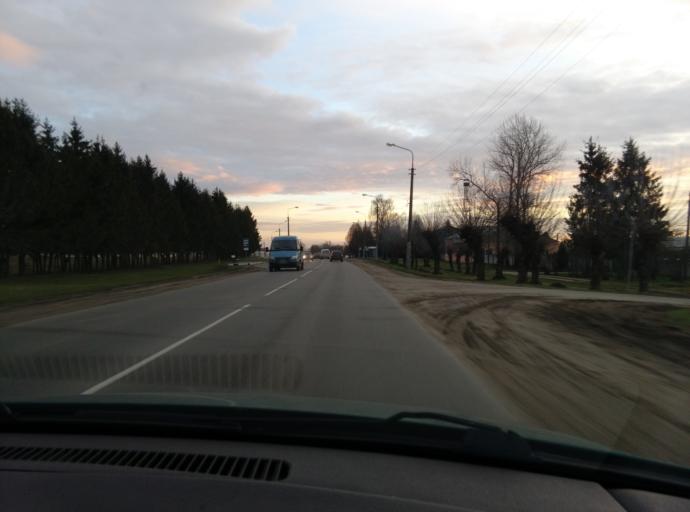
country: BY
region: Minsk
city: Horad Barysaw
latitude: 54.2676
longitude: 28.4991
